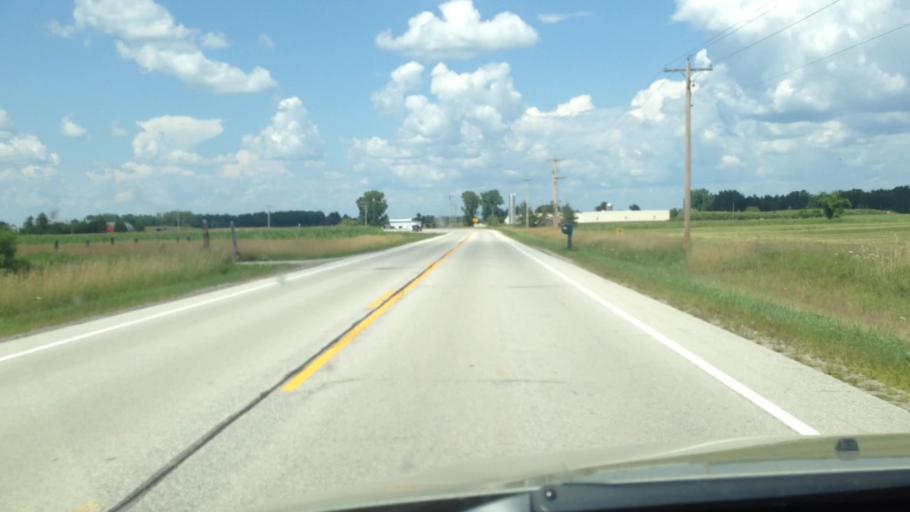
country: US
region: Wisconsin
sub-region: Brown County
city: Pulaski
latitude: 44.6552
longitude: -88.1809
